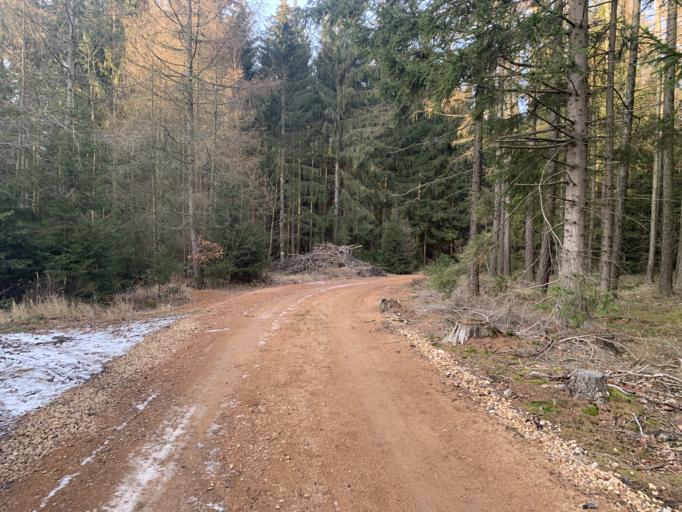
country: CZ
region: Central Bohemia
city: Komarov
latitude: 49.8173
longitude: 13.8075
